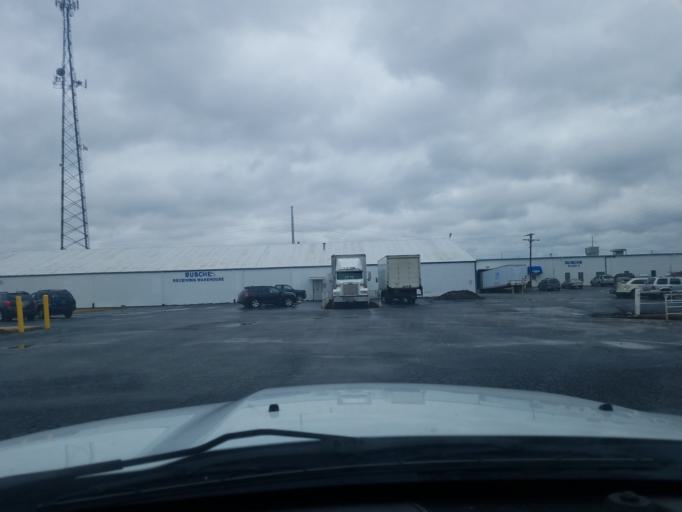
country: US
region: Indiana
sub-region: Noble County
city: Albion
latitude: 41.3966
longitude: -85.3941
